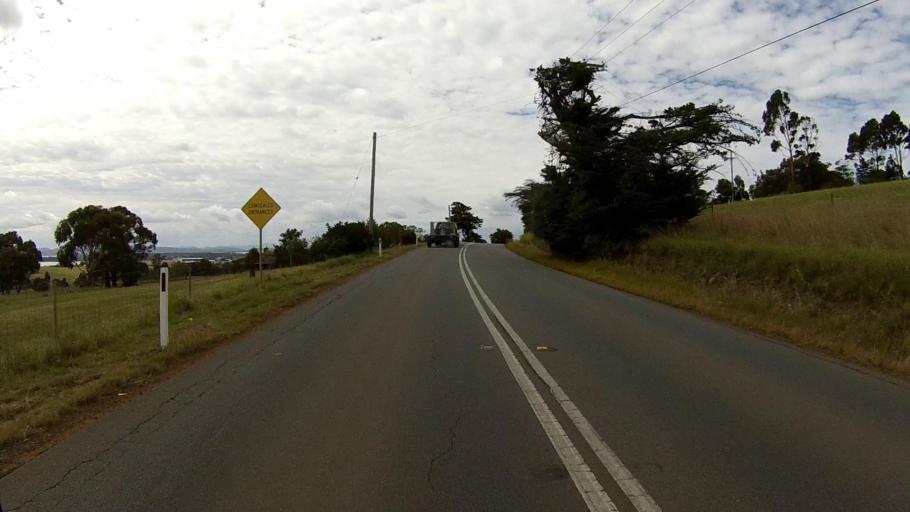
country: AU
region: Tasmania
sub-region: Clarence
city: Cambridge
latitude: -42.8239
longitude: 147.4471
